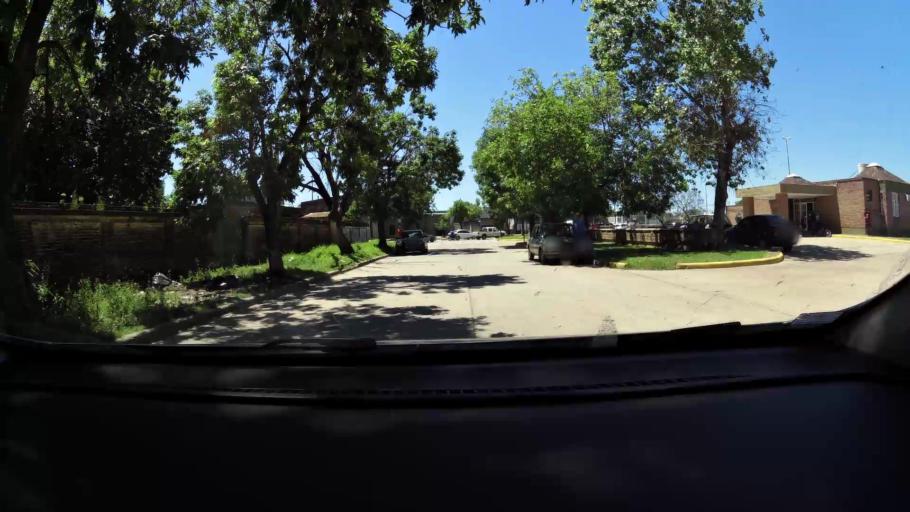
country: AR
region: Santa Fe
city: Santa Fe de la Vera Cruz
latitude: -31.6134
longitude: -60.7188
